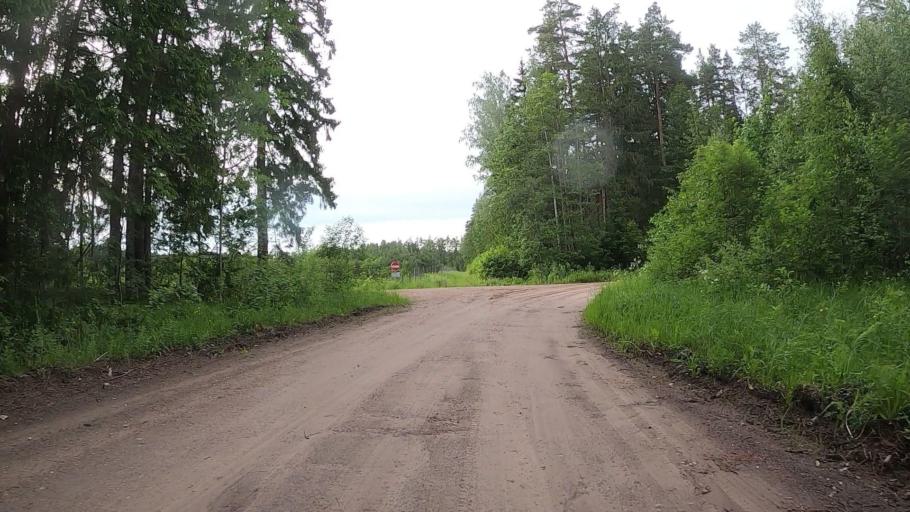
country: LV
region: Ozolnieku
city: Ozolnieki
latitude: 56.7265
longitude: 23.7887
